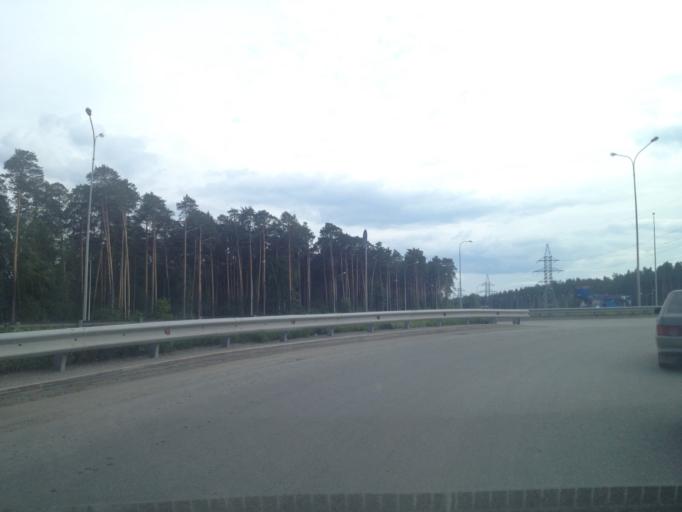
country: RU
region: Sverdlovsk
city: Sovkhoznyy
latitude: 56.7908
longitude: 60.5998
